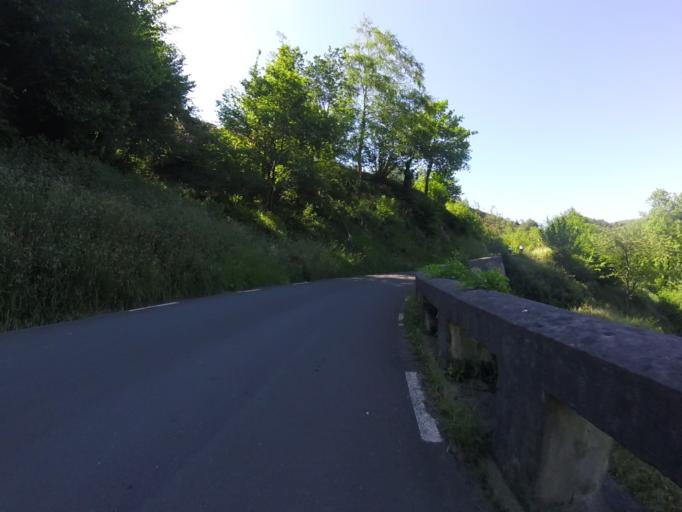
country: ES
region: Basque Country
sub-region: Provincia de Guipuzcoa
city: Beizama
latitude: 43.1328
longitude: -2.1952
